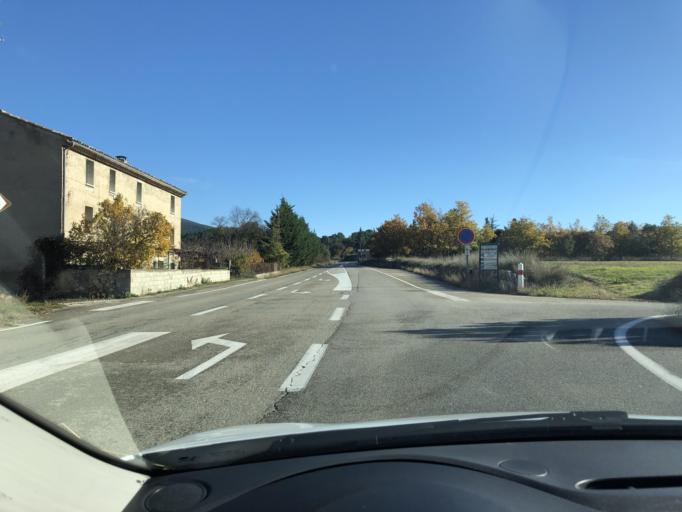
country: FR
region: Provence-Alpes-Cote d'Azur
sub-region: Departement du Vaucluse
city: Saignon
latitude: 43.9164
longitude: 5.4695
